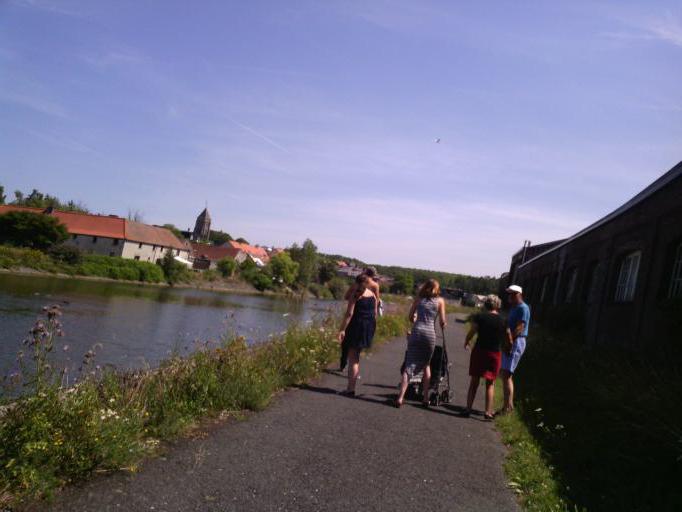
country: BE
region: Wallonia
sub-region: Province du Hainaut
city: Tournai
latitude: 50.5981
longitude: 3.4056
